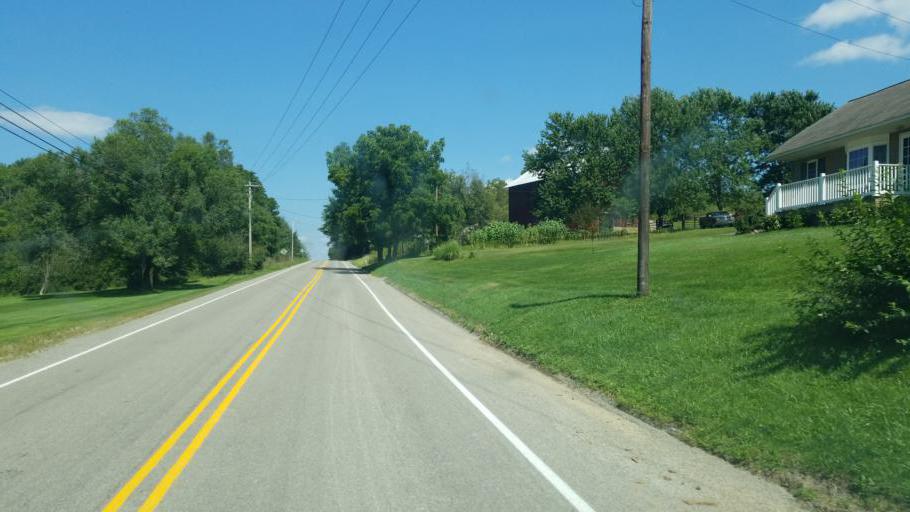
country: US
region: Pennsylvania
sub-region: Clarion County
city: Knox
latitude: 41.1106
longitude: -79.5971
